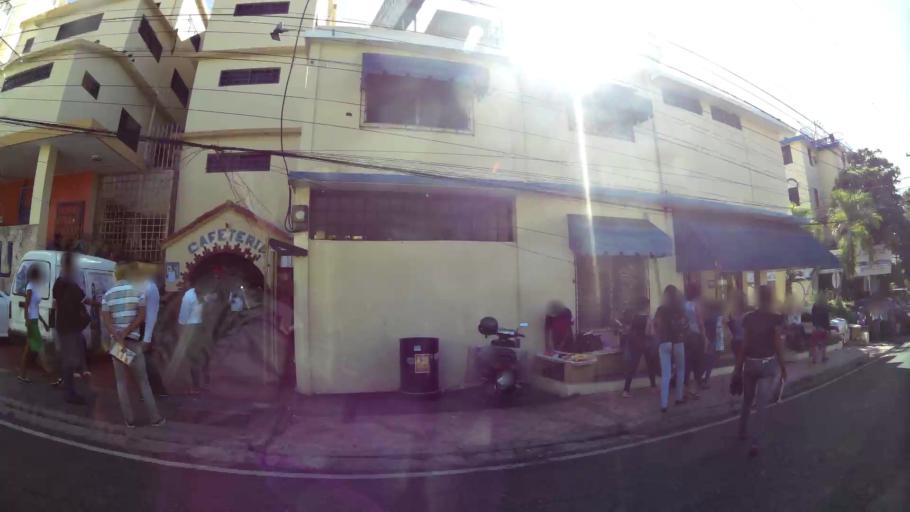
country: DO
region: Nacional
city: Ciudad Nueva
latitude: 18.4698
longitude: -69.8973
